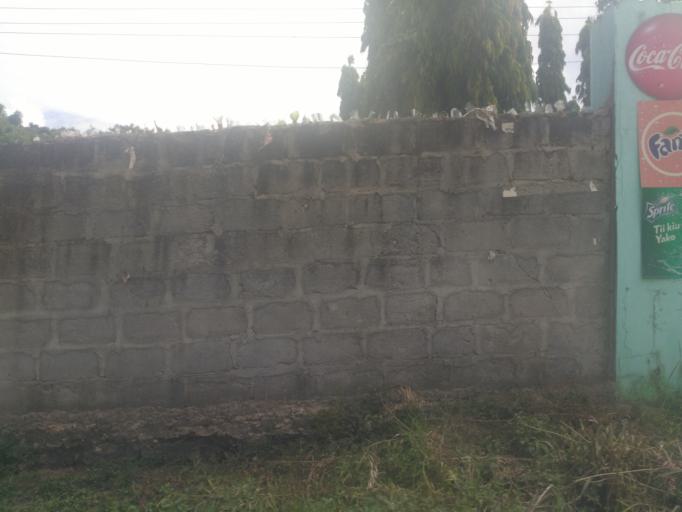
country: TZ
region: Zanzibar Urban/West
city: Zanzibar
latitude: -6.2358
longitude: 39.2133
